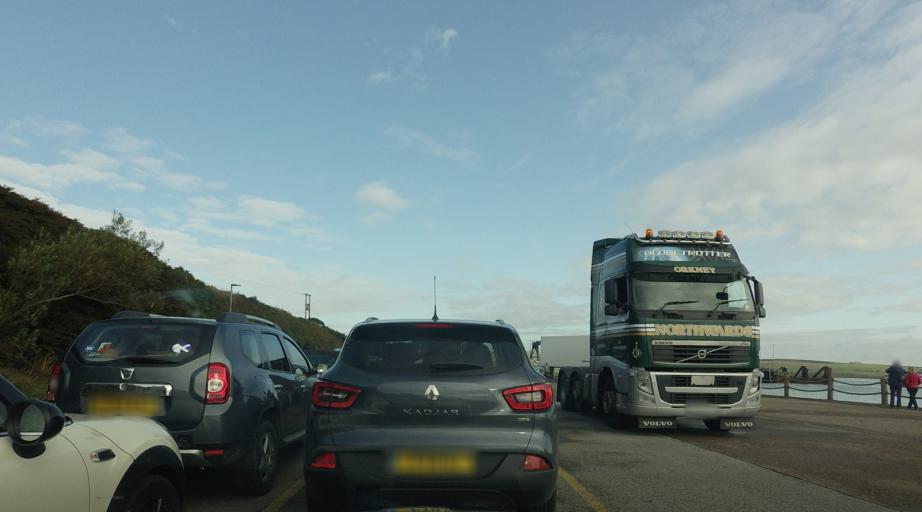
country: GB
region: Scotland
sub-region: Orkney Islands
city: Orkney
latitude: 58.8308
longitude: -2.9627
